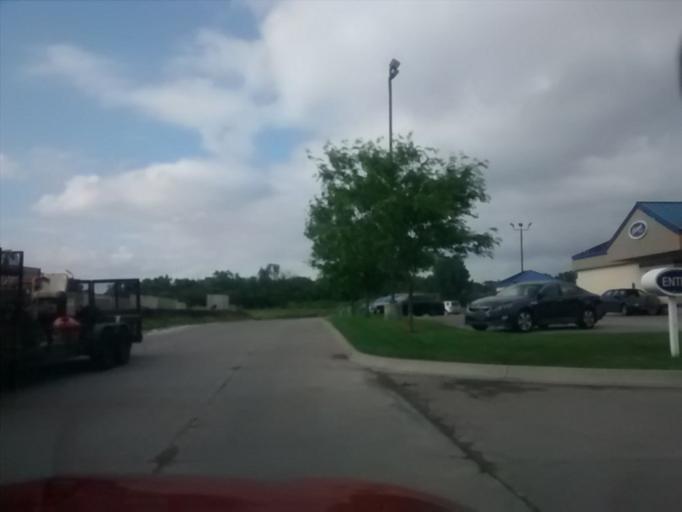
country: US
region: Nebraska
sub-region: Sarpy County
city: Offutt Air Force Base
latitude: 41.1476
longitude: -95.9684
